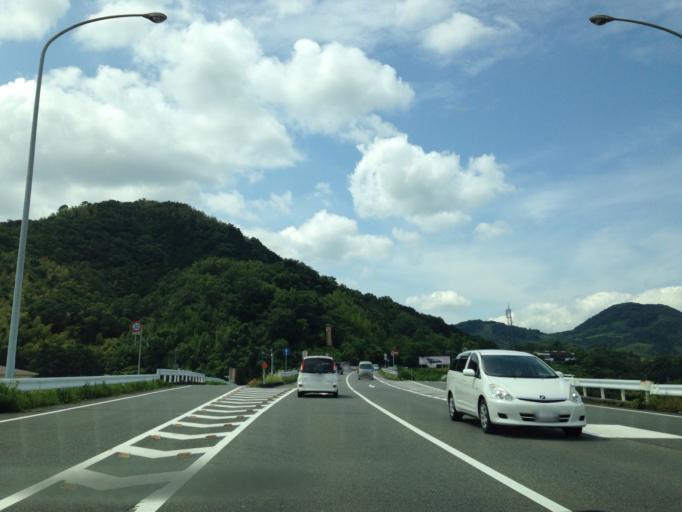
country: JP
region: Shizuoka
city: Mishima
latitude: 35.0539
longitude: 138.9241
